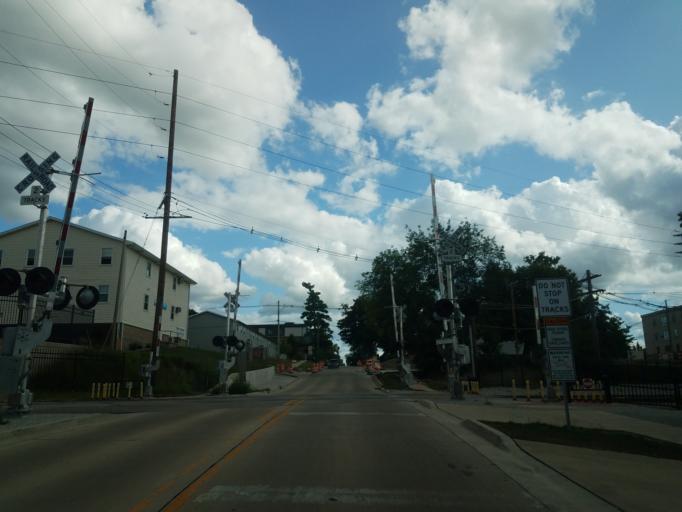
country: US
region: Illinois
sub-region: McLean County
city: Normal
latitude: 40.5073
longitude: -88.9871
